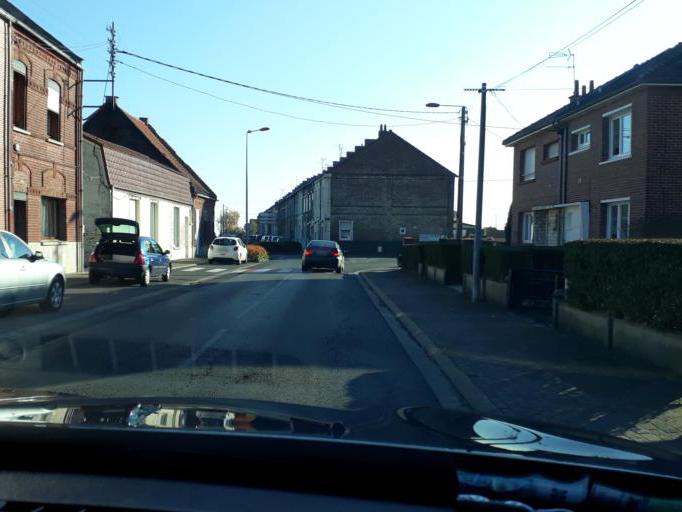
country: FR
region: Nord-Pas-de-Calais
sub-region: Departement du Nord
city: Emerchicourt
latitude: 50.3146
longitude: 3.2562
